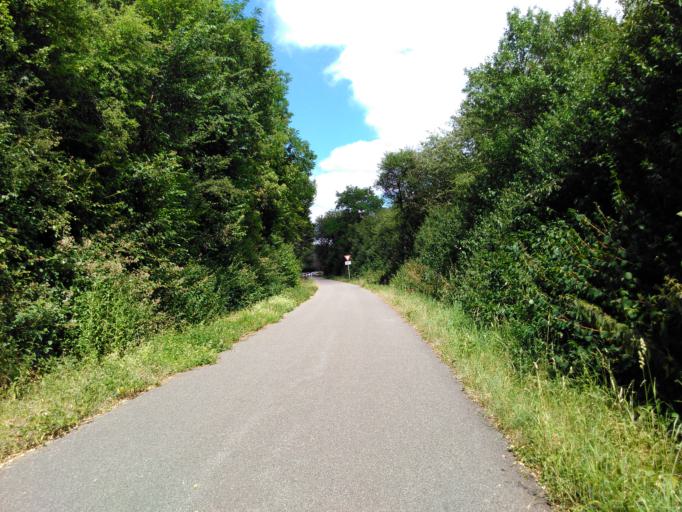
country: LU
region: Luxembourg
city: Hautcharage
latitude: 49.5752
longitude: 5.8938
